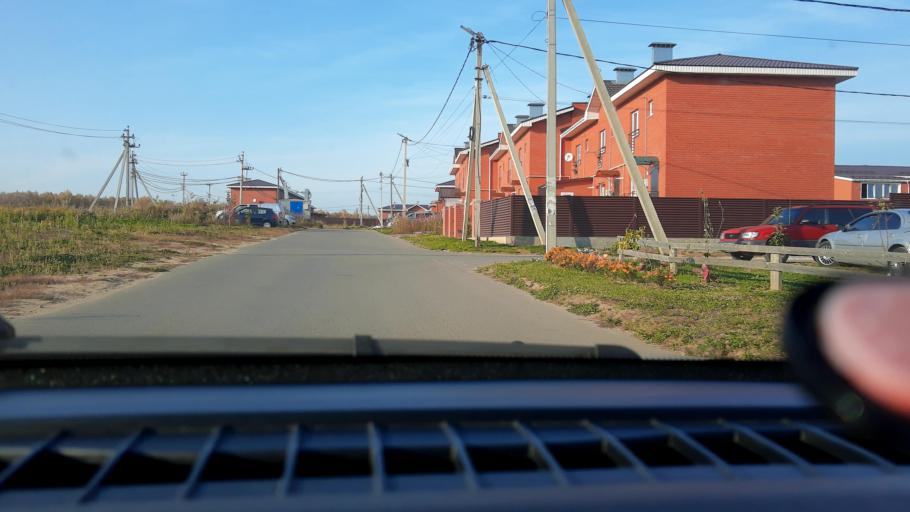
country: RU
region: Nizjnij Novgorod
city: Afonino
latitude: 56.2149
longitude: 44.0845
